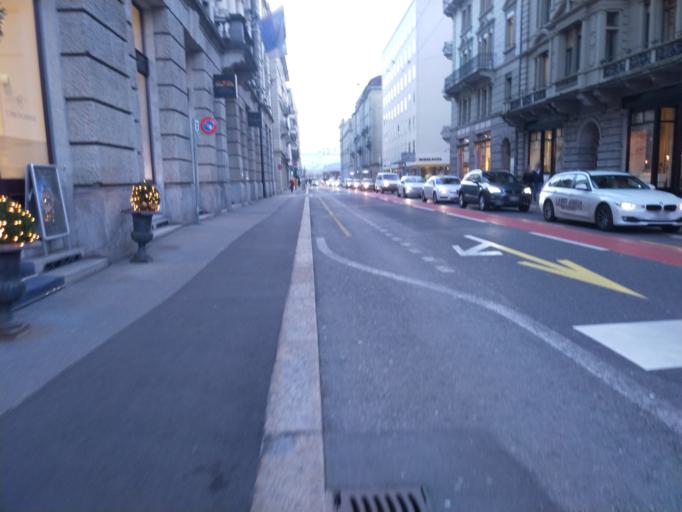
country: CH
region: Lucerne
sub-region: Lucerne-Stadt District
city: Luzern
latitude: 47.0565
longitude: 8.3111
